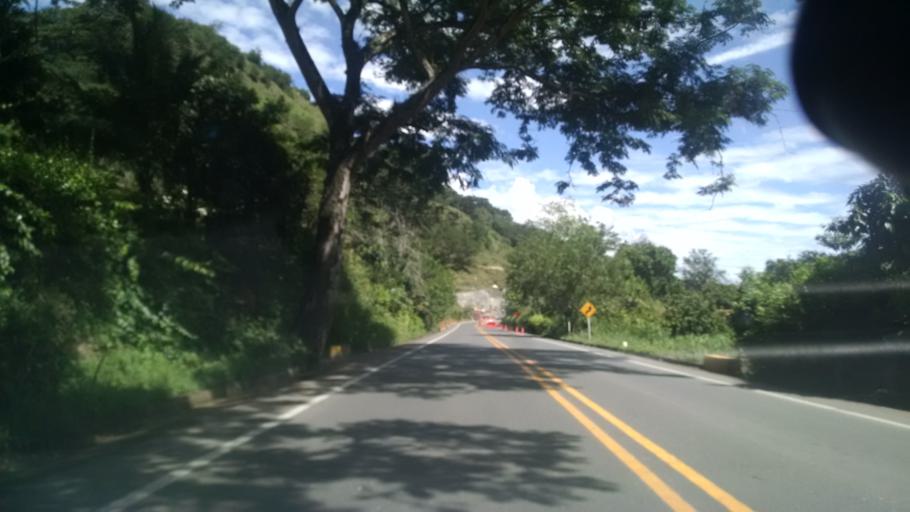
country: CO
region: Caldas
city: Filadelfia
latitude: 5.3588
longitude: -75.6166
